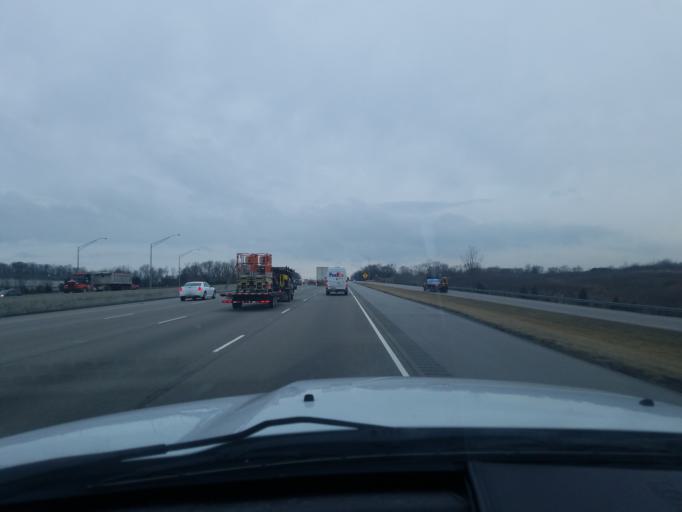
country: US
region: Ohio
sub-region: Warren County
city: Franklin
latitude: 39.5413
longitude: -84.2962
